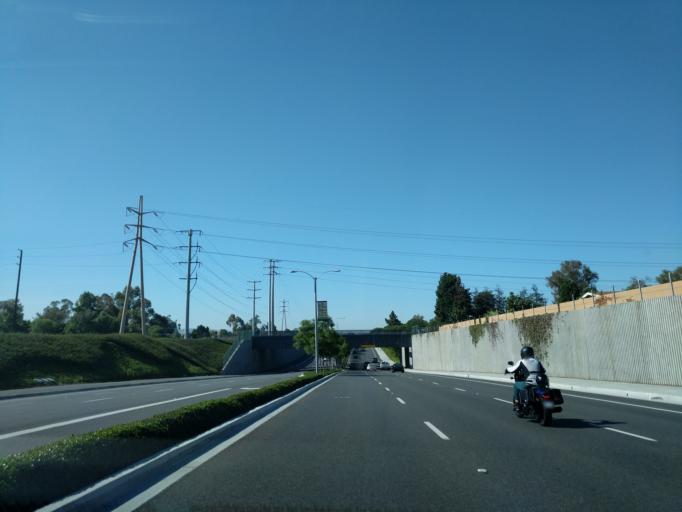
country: US
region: California
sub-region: Orange County
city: Irvine
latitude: 33.6861
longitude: -117.7723
